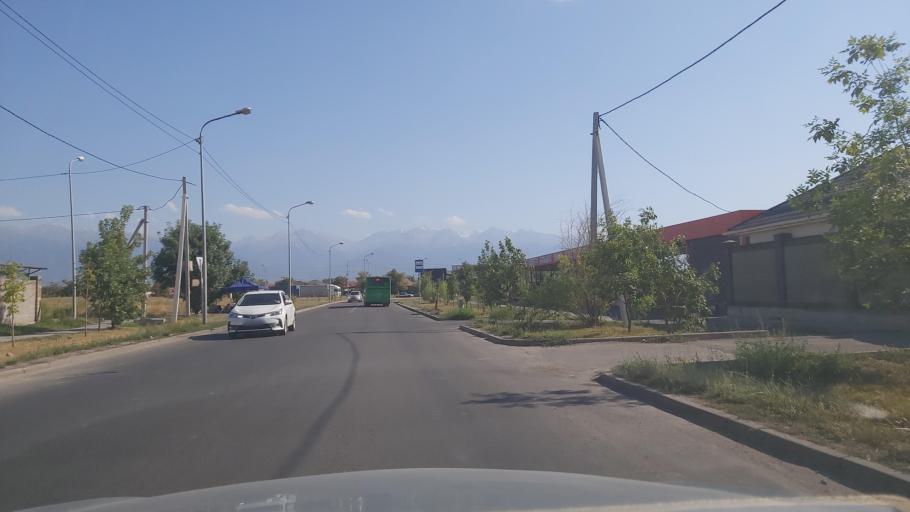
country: KZ
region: Almaty Oblysy
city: Burunday
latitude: 43.3153
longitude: 76.8423
